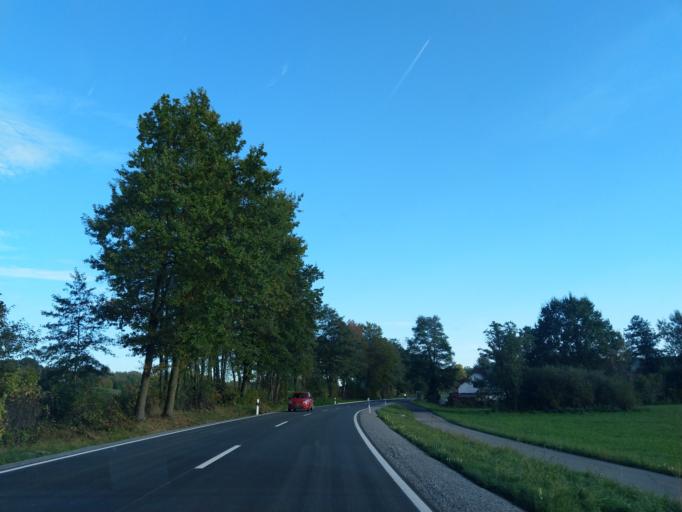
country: DE
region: Bavaria
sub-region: Lower Bavaria
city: Offenberg
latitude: 48.8704
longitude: 12.8557
